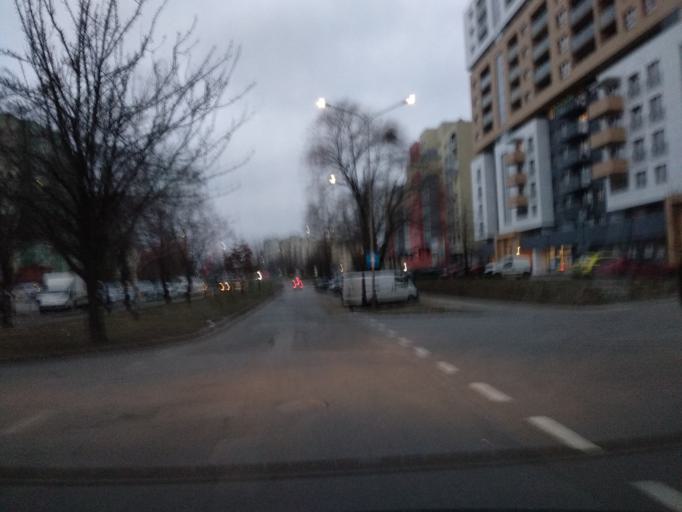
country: PL
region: Lower Silesian Voivodeship
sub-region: Powiat wroclawski
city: Wroclaw
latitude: 51.1268
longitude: 16.9691
